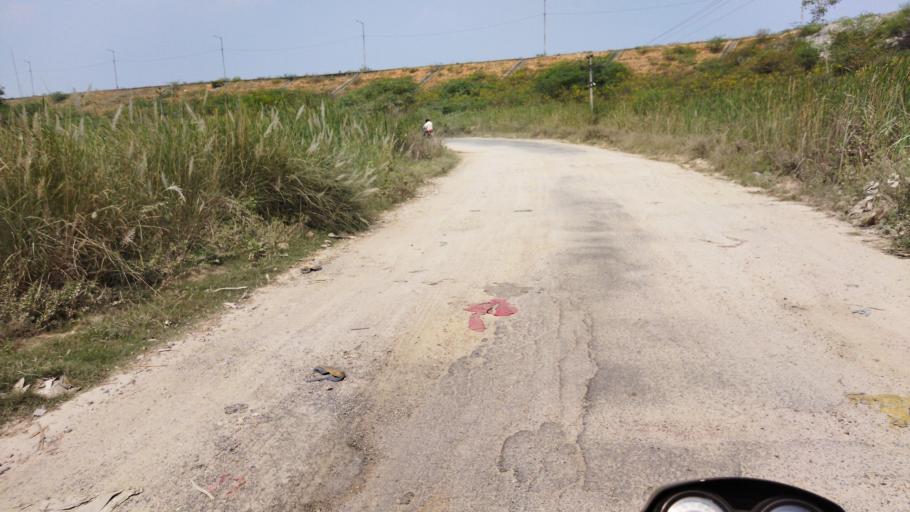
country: IN
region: Telangana
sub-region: Nalgonda
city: Nalgonda
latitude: 17.0764
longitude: 79.3143
